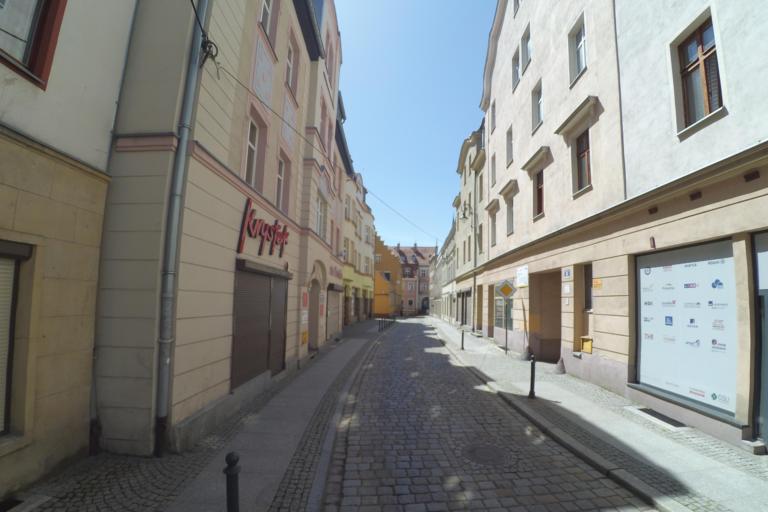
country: PL
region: Lower Silesian Voivodeship
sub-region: Powiat walbrzyski
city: Walbrzych
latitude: 50.7671
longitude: 16.2831
